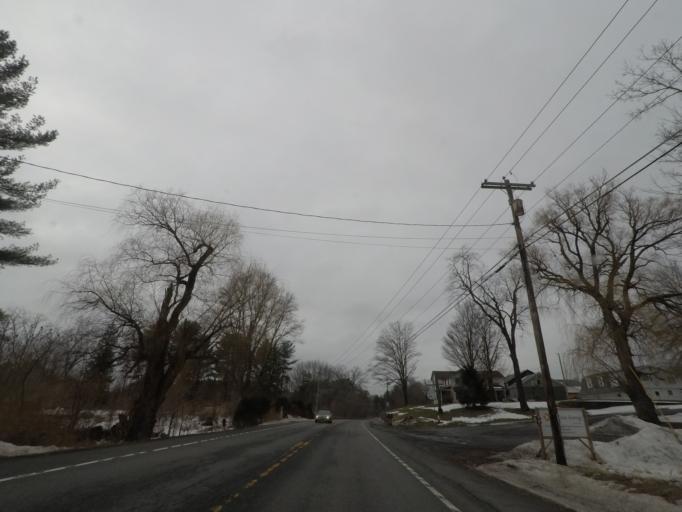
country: US
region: New York
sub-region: Schenectady County
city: Rotterdam
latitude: 42.7296
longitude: -73.9714
